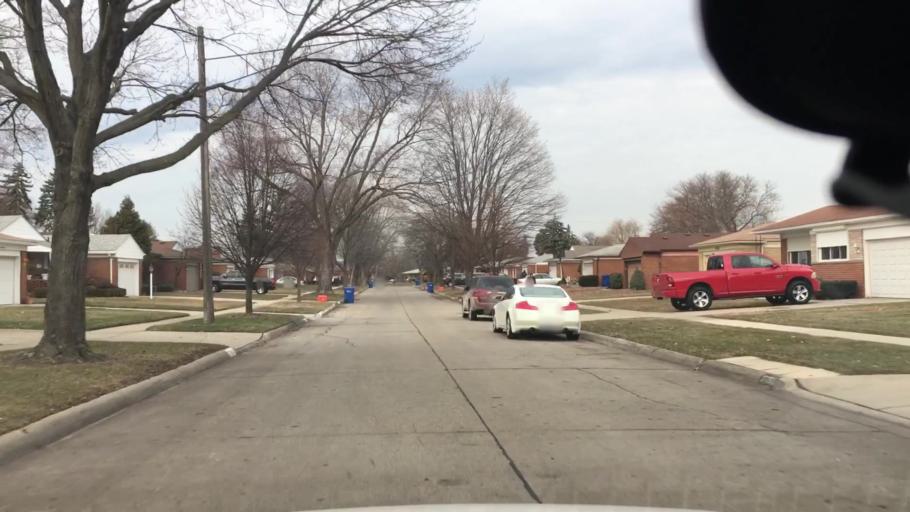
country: US
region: Michigan
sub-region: Oakland County
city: Madison Heights
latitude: 42.4928
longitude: -83.0712
